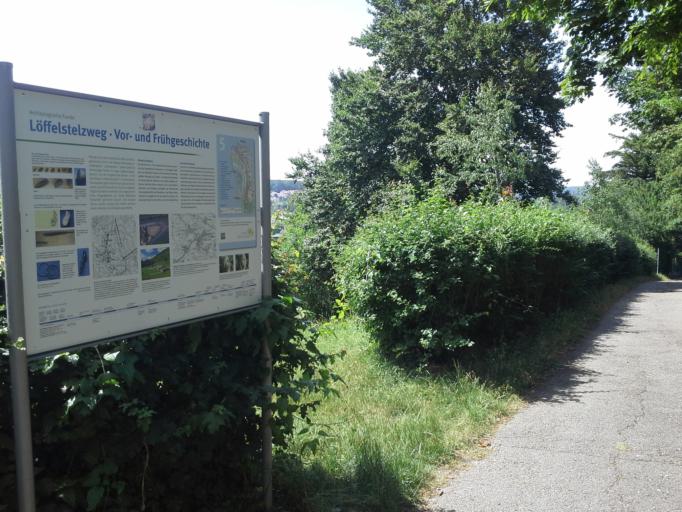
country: DE
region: Baden-Wuerttemberg
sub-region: Karlsruhe Region
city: Muhlacker
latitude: 48.9446
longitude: 8.8450
